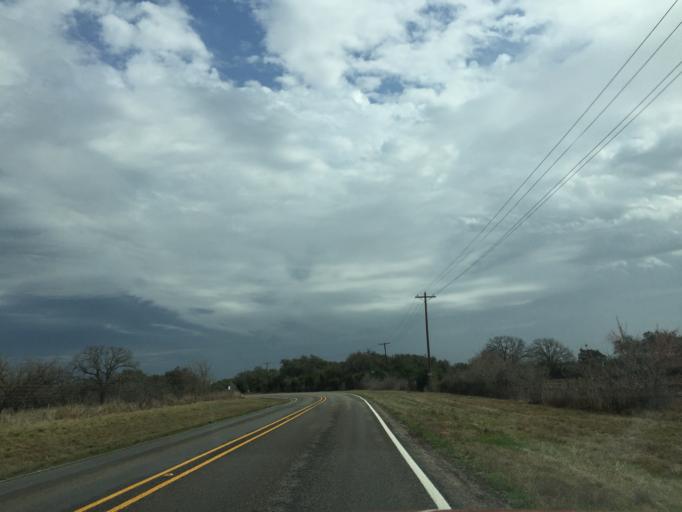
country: US
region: Texas
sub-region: Burnet County
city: Bertram
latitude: 30.6522
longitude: -97.9686
